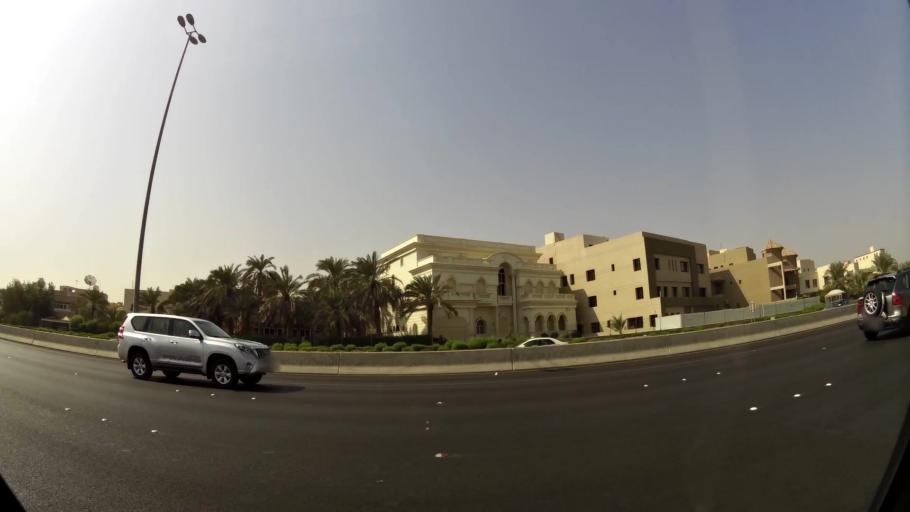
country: KW
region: Muhafazat Hawalli
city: Hawalli
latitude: 29.3367
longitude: 48.0032
